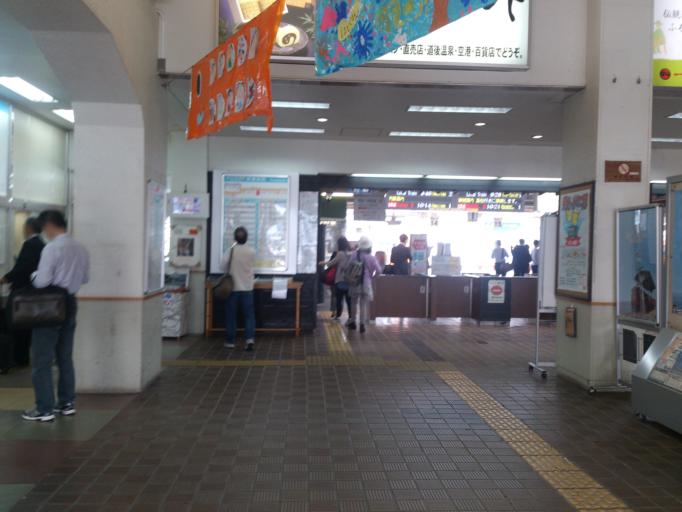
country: JP
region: Ehime
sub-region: Shikoku-chuo Shi
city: Matsuyama
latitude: 33.8402
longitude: 132.7517
